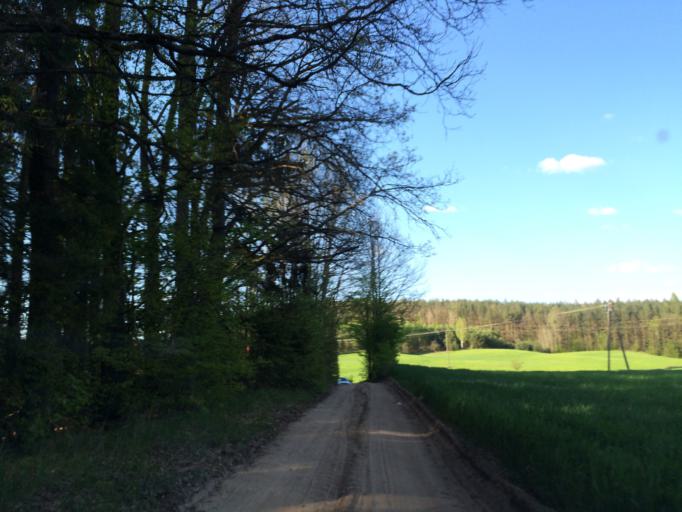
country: PL
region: Warmian-Masurian Voivodeship
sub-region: Powiat dzialdowski
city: Lidzbark
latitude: 53.2316
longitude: 19.7658
